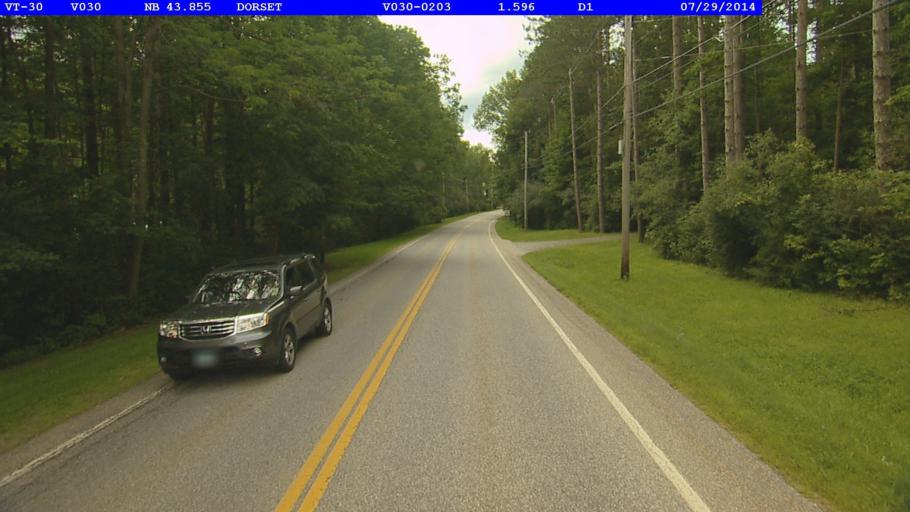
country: US
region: Vermont
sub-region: Bennington County
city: Manchester Center
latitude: 43.2333
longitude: -73.0808
